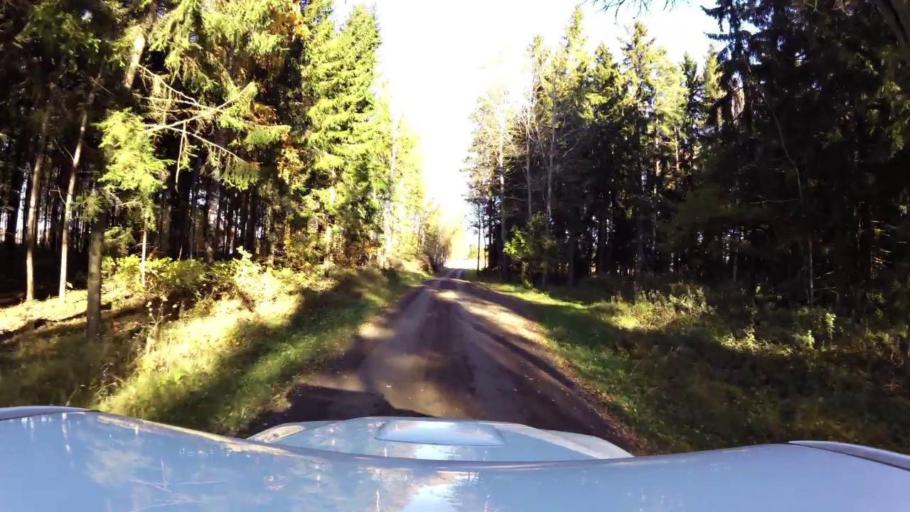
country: SE
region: OEstergoetland
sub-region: Linkopings Kommun
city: Ljungsbro
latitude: 58.4981
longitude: 15.3862
